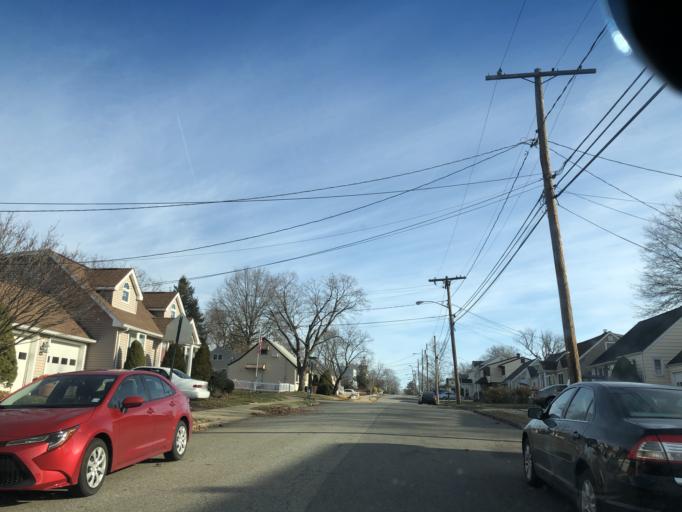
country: US
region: New Jersey
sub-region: Bergen County
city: Fair Lawn
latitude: 40.9312
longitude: -74.1372
